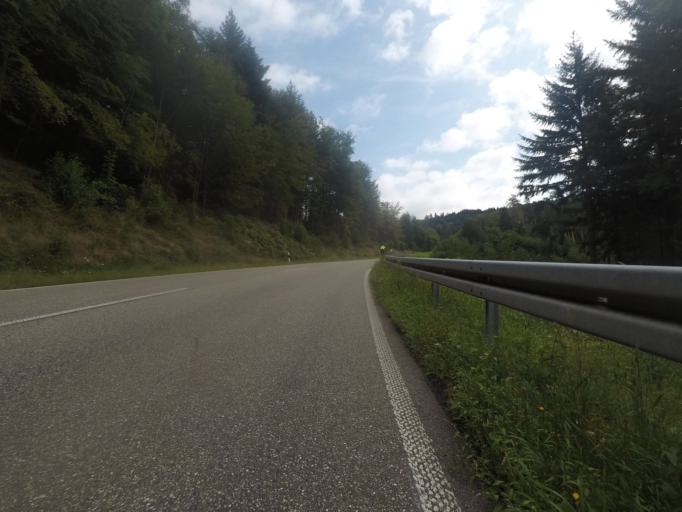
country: DE
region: Baden-Wuerttemberg
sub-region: Karlsruhe Region
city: Gaggenau
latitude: 48.8322
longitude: 8.3640
